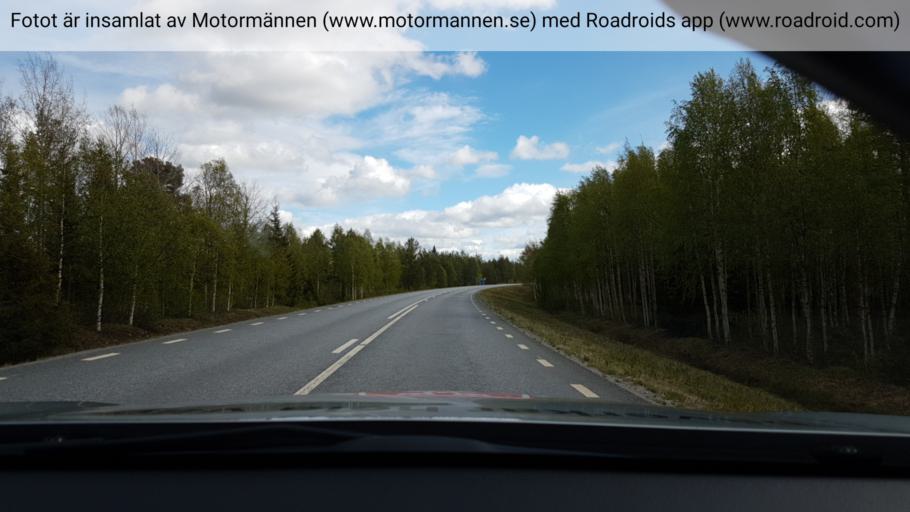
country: SE
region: Vaesterbotten
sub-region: Asele Kommun
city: Insjon
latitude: 64.1921
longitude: 17.7748
